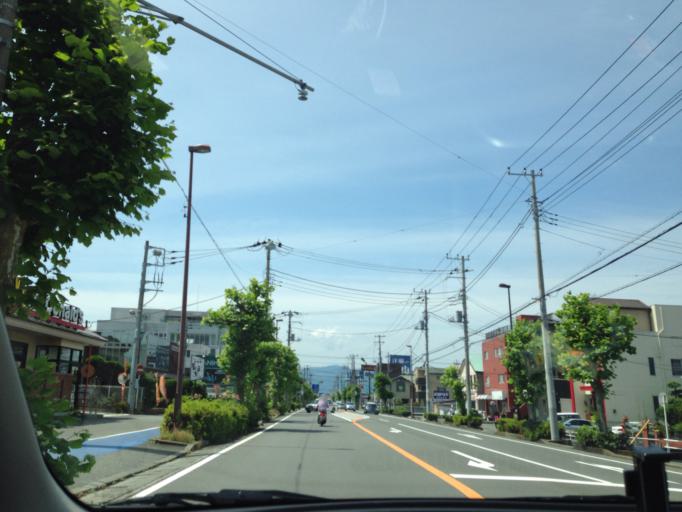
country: JP
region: Shizuoka
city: Numazu
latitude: 35.1117
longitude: 138.8664
